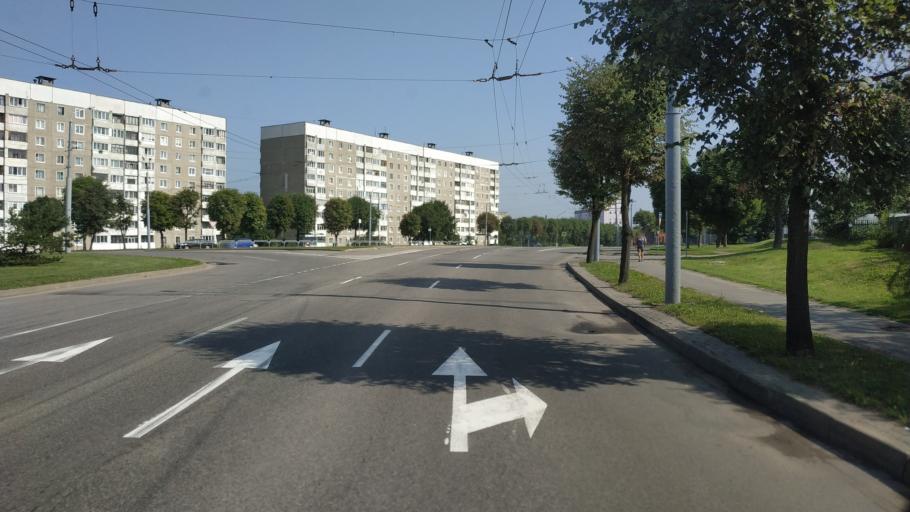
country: BY
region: Mogilev
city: Mahilyow
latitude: 53.8984
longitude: 30.2954
